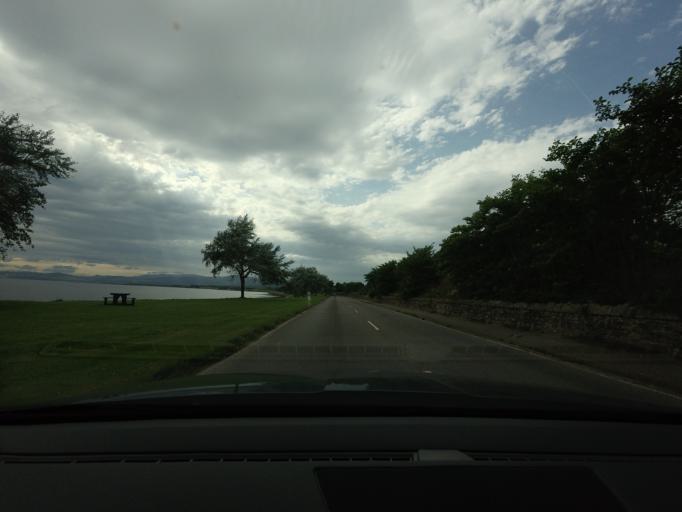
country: GB
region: Scotland
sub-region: Highland
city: Invergordon
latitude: 57.6904
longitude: -4.1848
